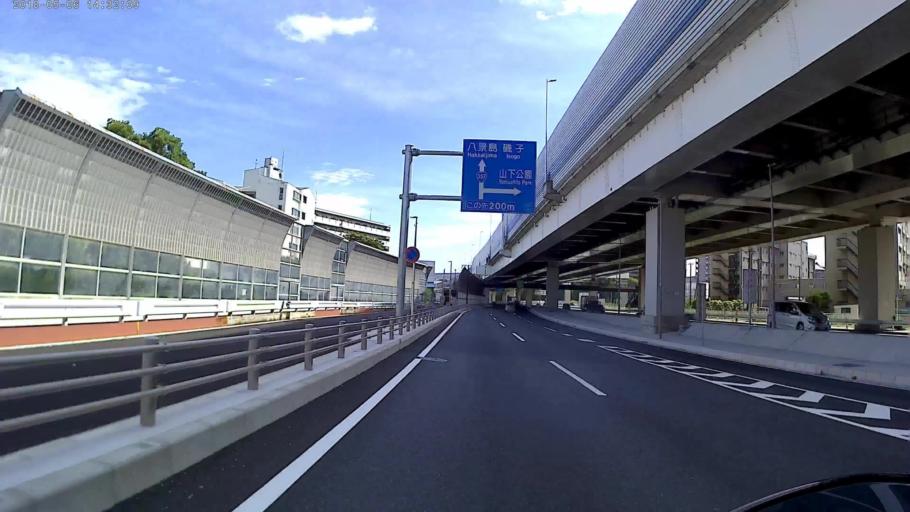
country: JP
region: Kanagawa
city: Yokohama
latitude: 35.4279
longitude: 139.6715
